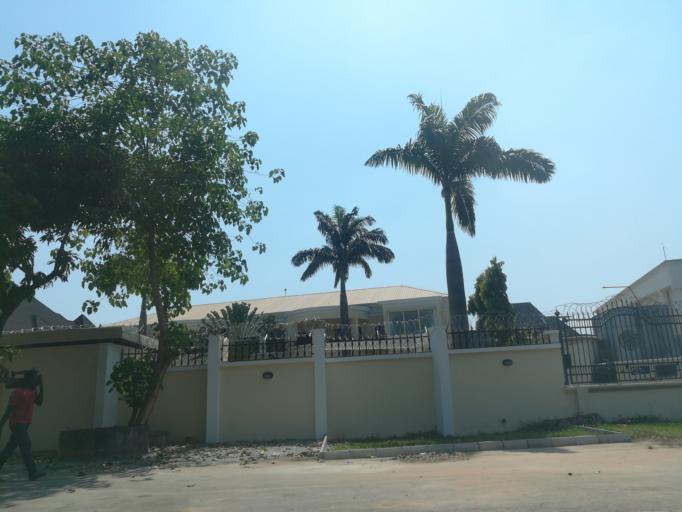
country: NG
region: Abuja Federal Capital Territory
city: Abuja
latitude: 9.0740
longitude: 7.4388
